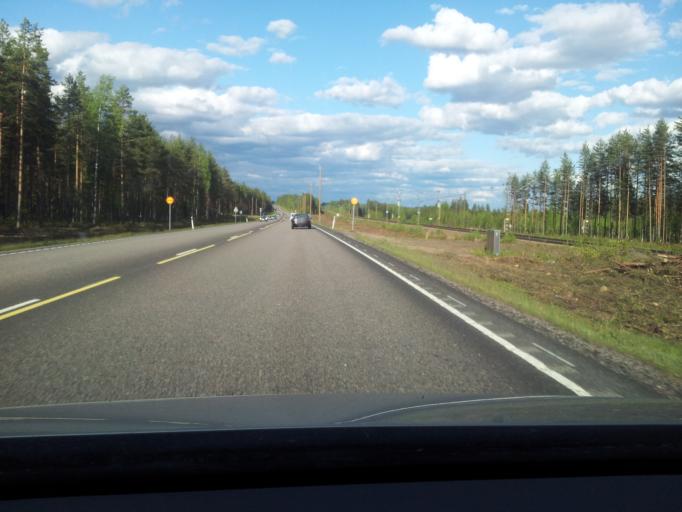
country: FI
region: South Karelia
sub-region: Lappeenranta
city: Taavetti
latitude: 60.9084
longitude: 27.2897
